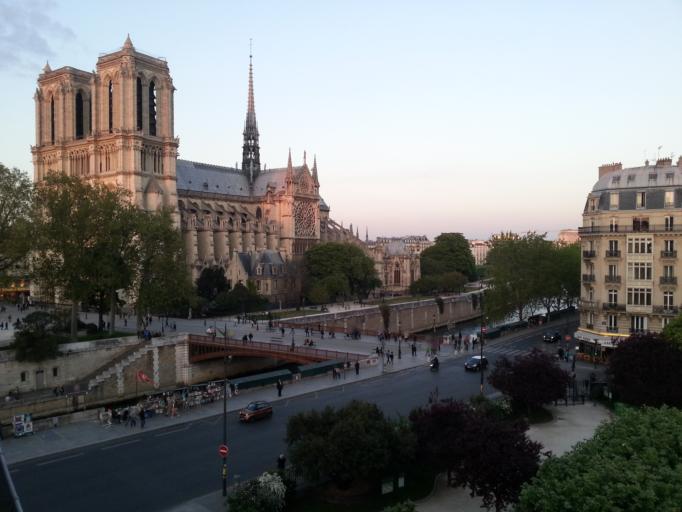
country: FR
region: Ile-de-France
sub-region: Paris
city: Paris
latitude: 48.8524
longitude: 2.3472
